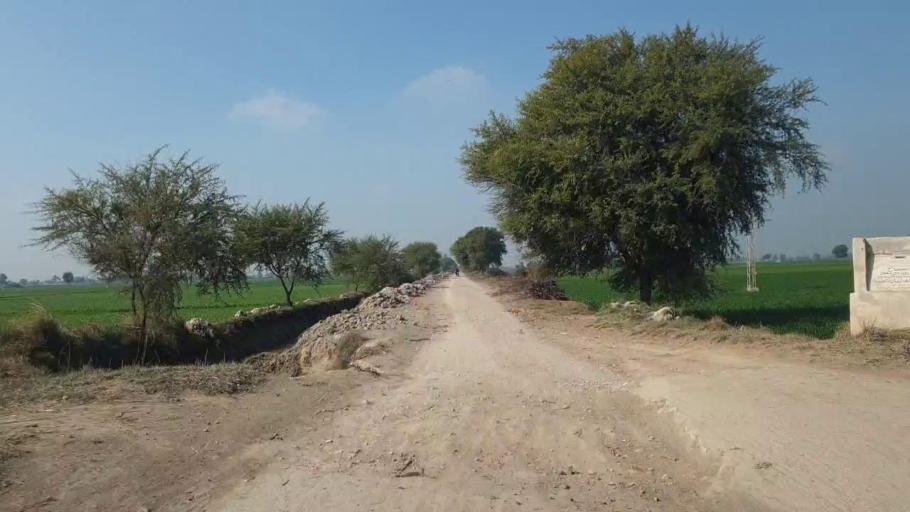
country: PK
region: Sindh
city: Shahdadpur
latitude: 26.0238
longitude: 68.5845
